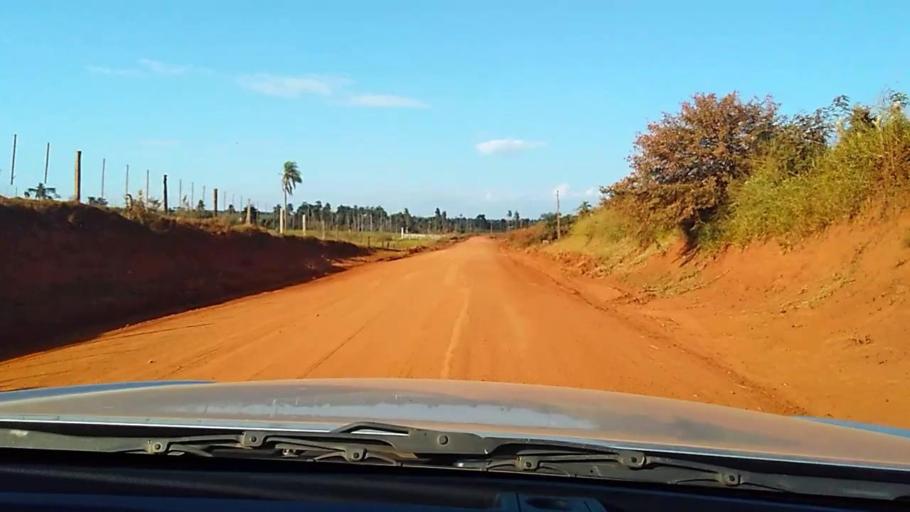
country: PY
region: Alto Parana
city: Doctor Juan Leon Mallorquin
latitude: -25.7019
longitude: -55.3817
